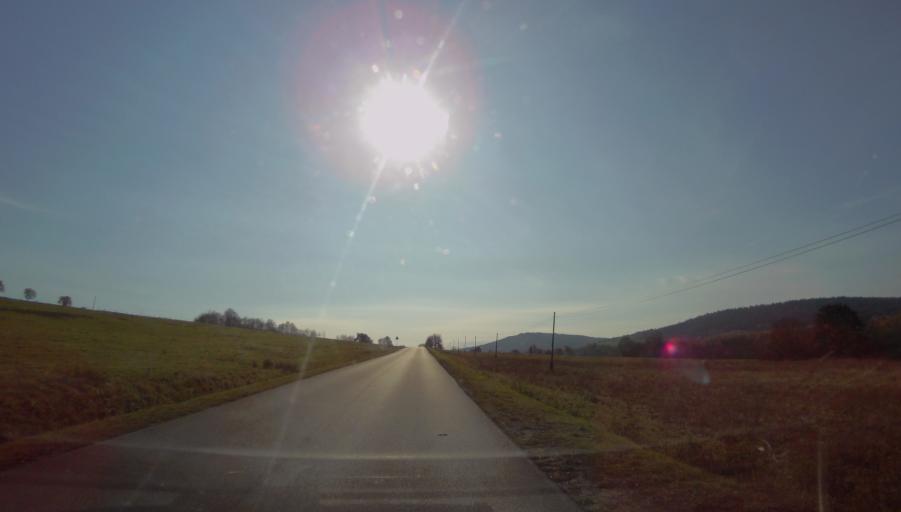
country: PL
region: Subcarpathian Voivodeship
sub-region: Powiat sanocki
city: Komancza
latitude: 49.3000
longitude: 22.0564
